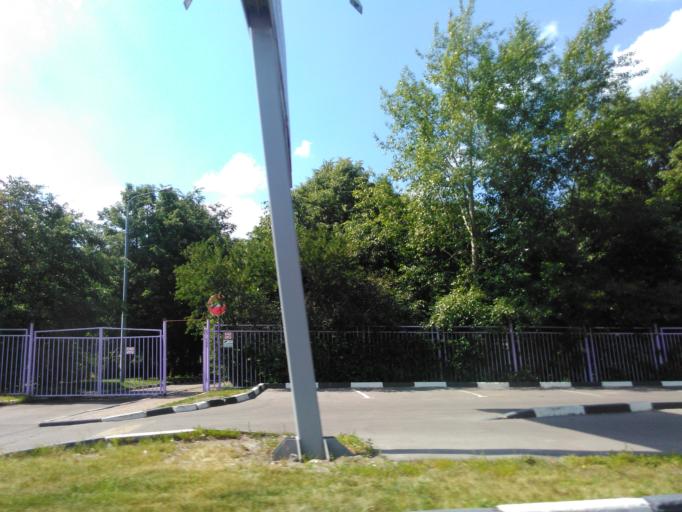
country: RU
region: Moscow
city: Zyuzino
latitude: 55.6667
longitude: 37.5815
